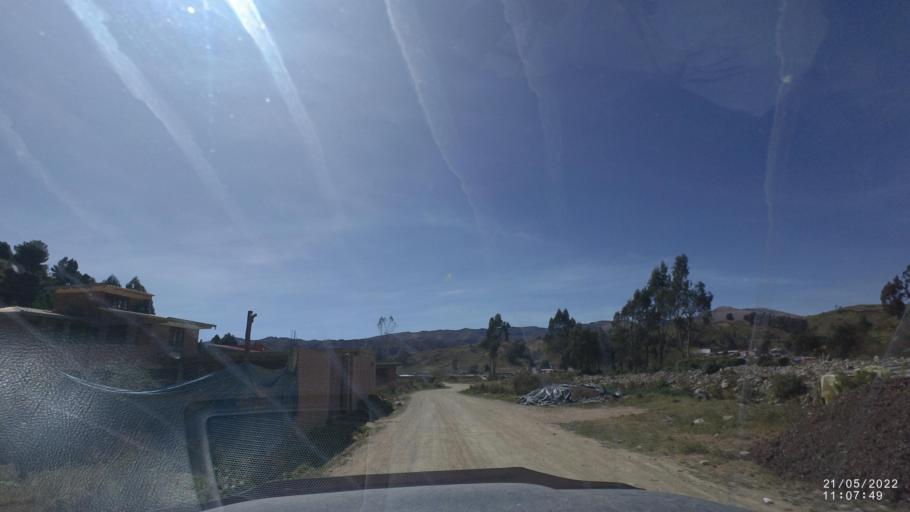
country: BO
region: Cochabamba
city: Colomi
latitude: -17.3095
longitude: -65.9153
